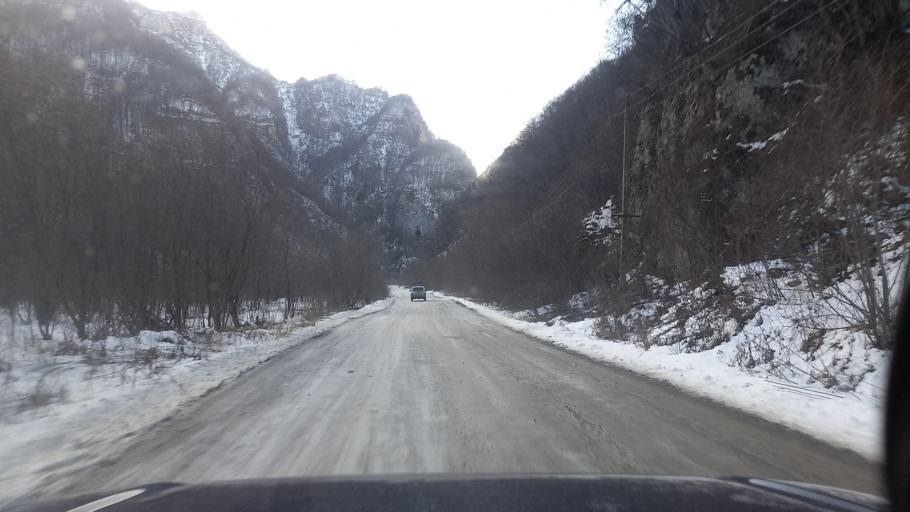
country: RU
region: North Ossetia
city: Gizel'
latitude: 42.9044
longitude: 44.5295
